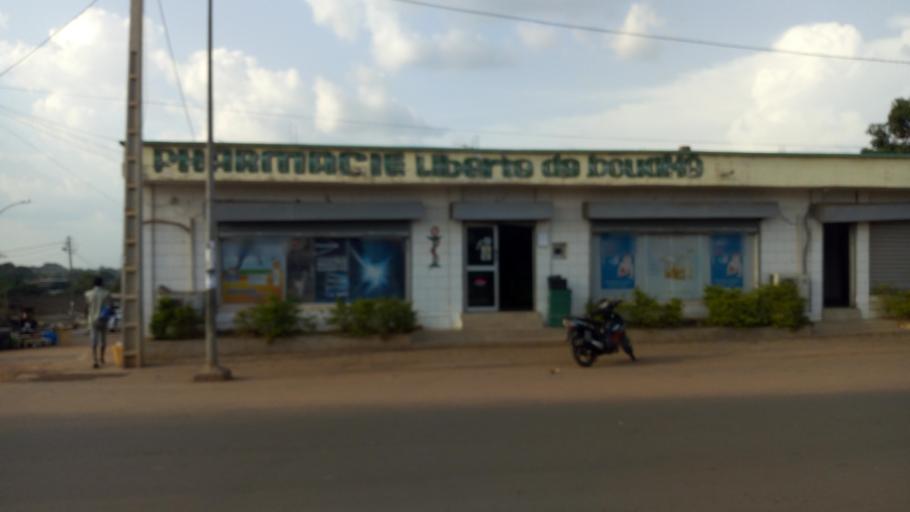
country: CI
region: Vallee du Bandama
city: Bouake
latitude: 7.6917
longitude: -5.0145
